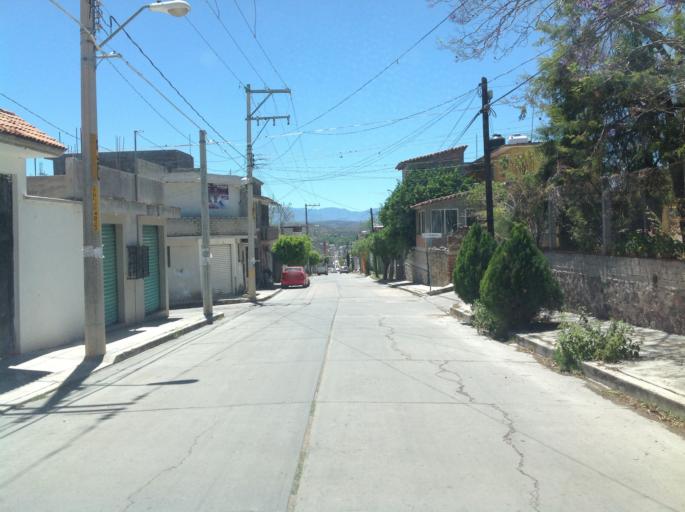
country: MX
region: Oaxaca
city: Ciudad de Huajuapam de Leon
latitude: 17.8143
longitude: -97.7743
